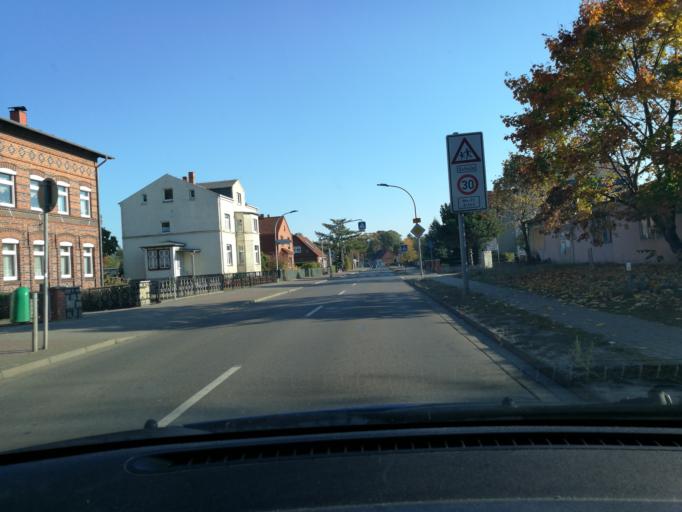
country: DE
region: Mecklenburg-Vorpommern
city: Domitz
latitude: 53.1365
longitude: 11.2668
